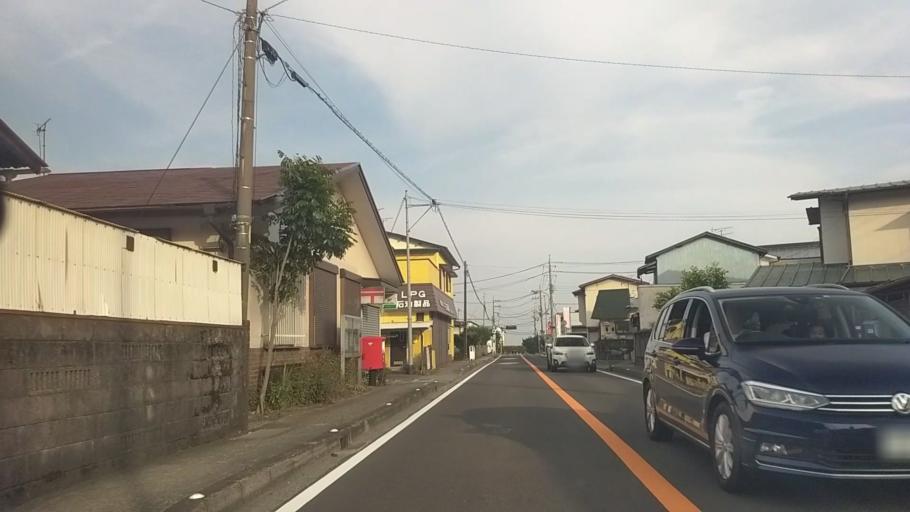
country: JP
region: Kanagawa
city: Odawara
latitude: 35.3524
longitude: 139.0929
